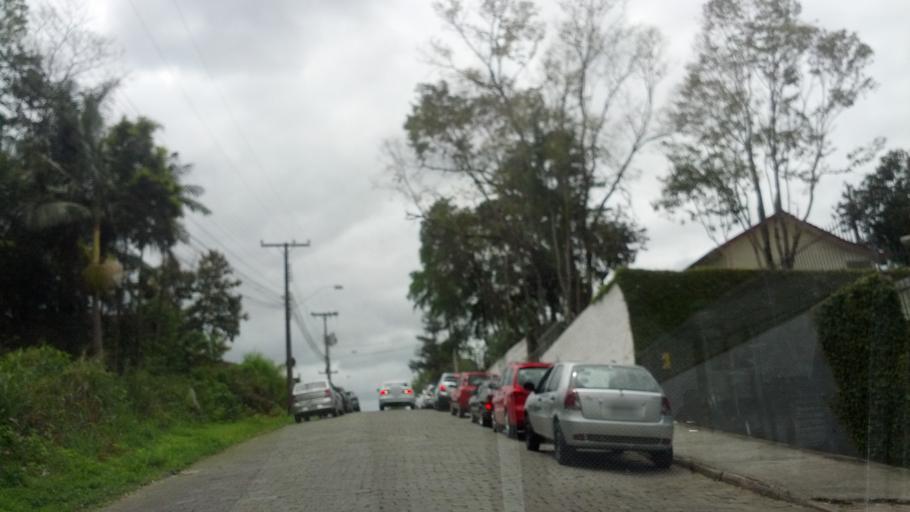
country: BR
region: Santa Catarina
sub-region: Blumenau
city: Blumenau
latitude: -26.9076
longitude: -49.0912
